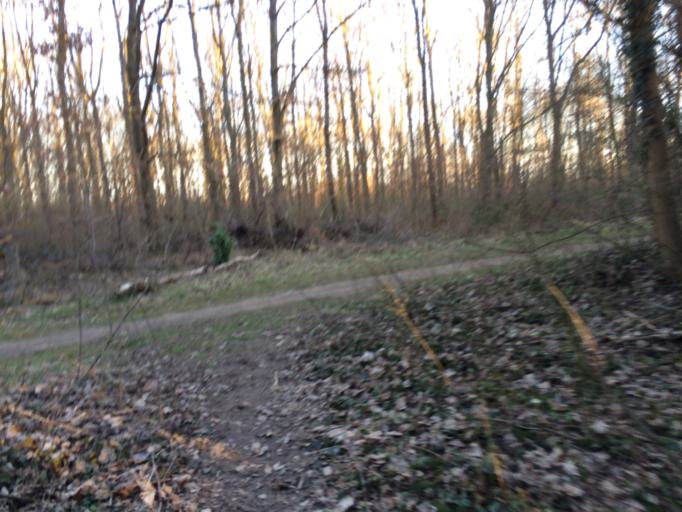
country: FR
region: Ile-de-France
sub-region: Departement de l'Essonne
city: Villebon-sur-Yvette
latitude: 48.7113
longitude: 2.2233
